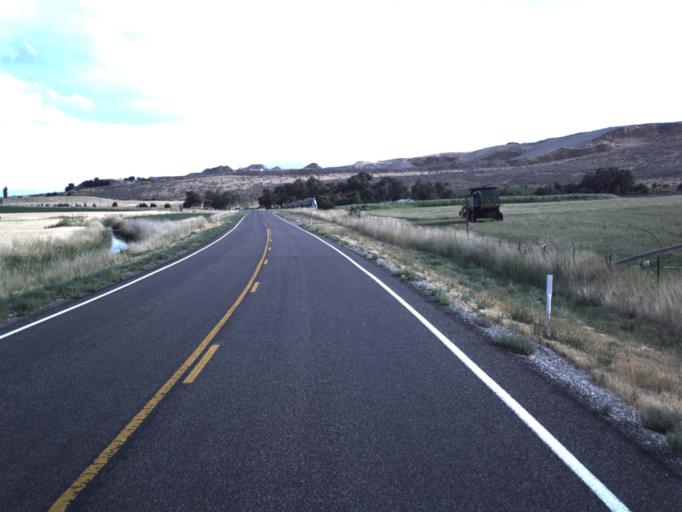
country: US
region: Utah
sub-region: Cache County
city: Benson
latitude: 41.8861
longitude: -111.9509
